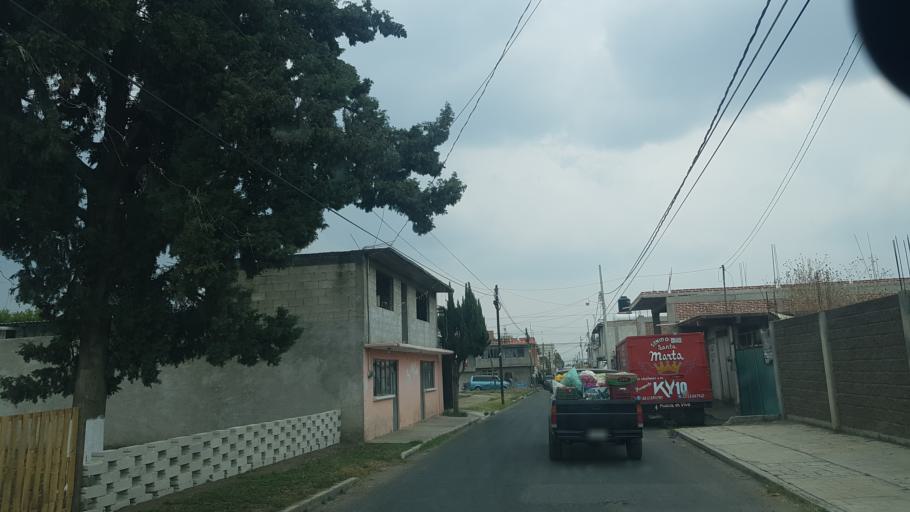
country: MX
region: Puebla
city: Huejotzingo
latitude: 19.1596
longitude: -98.4140
